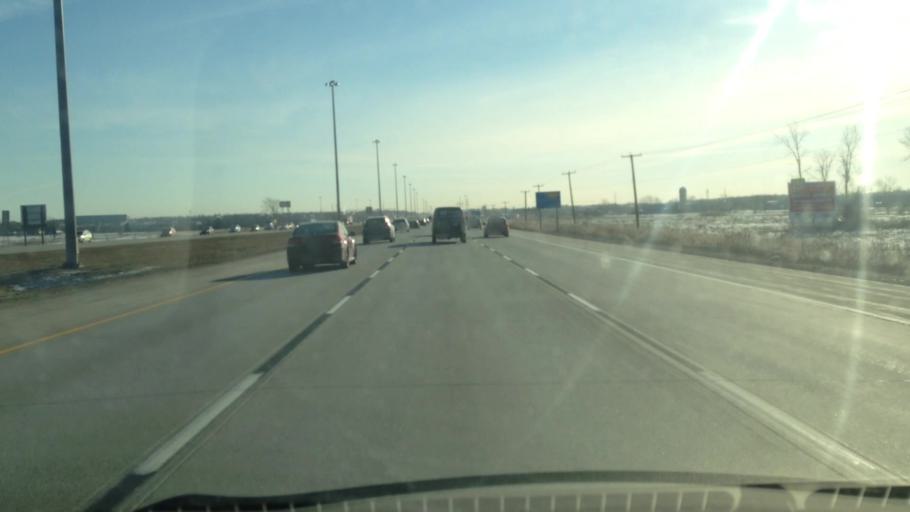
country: CA
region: Quebec
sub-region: Laurentides
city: Blainville
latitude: 45.7003
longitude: -73.9492
